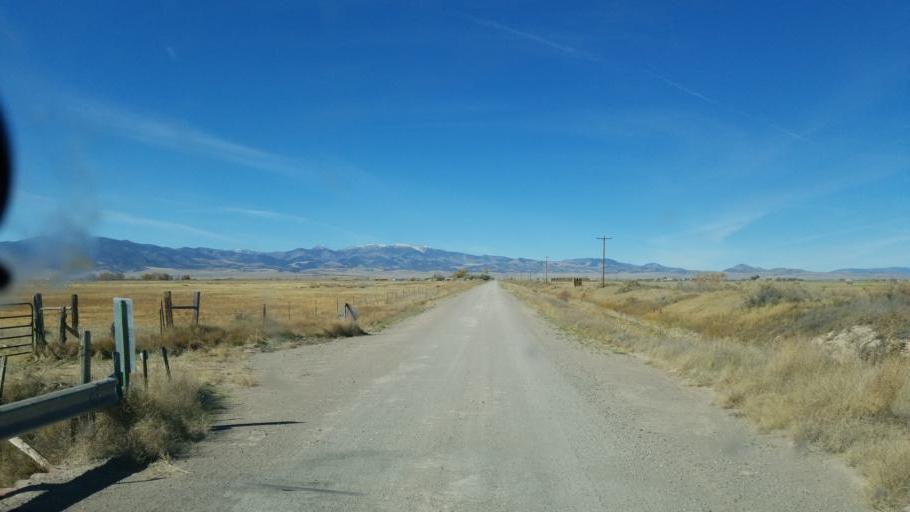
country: US
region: Colorado
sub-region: Rio Grande County
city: Monte Vista
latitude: 37.5313
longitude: -106.0739
